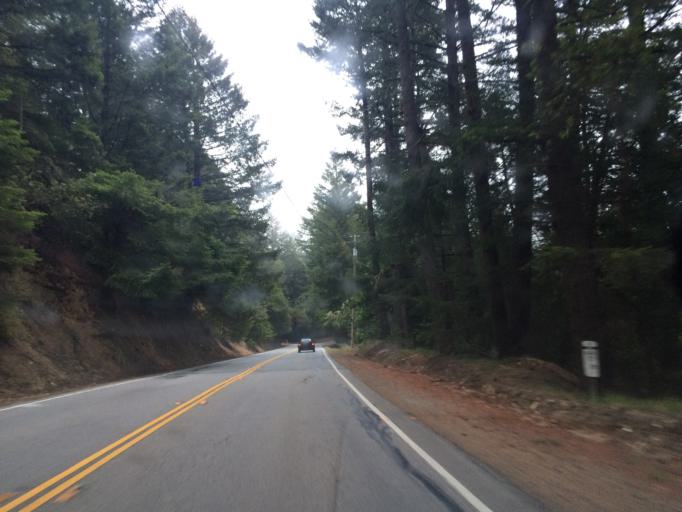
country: US
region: California
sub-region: Santa Cruz County
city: Boulder Creek
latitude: 37.2408
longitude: -122.1521
